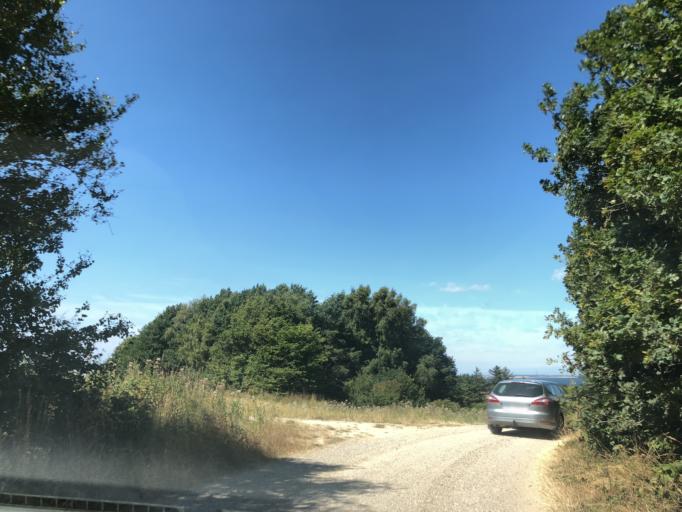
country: DK
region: North Denmark
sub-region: Morso Kommune
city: Nykobing Mors
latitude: 56.8372
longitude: 9.0034
